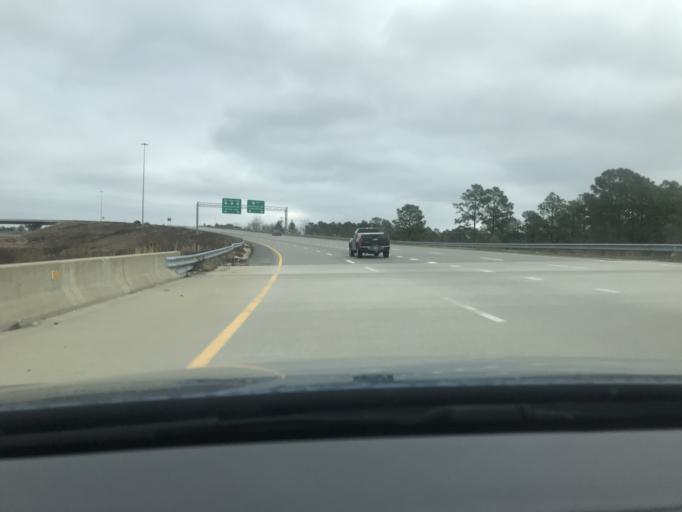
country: US
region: North Carolina
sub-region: Cumberland County
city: Spring Lake
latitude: 35.1180
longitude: -78.9431
